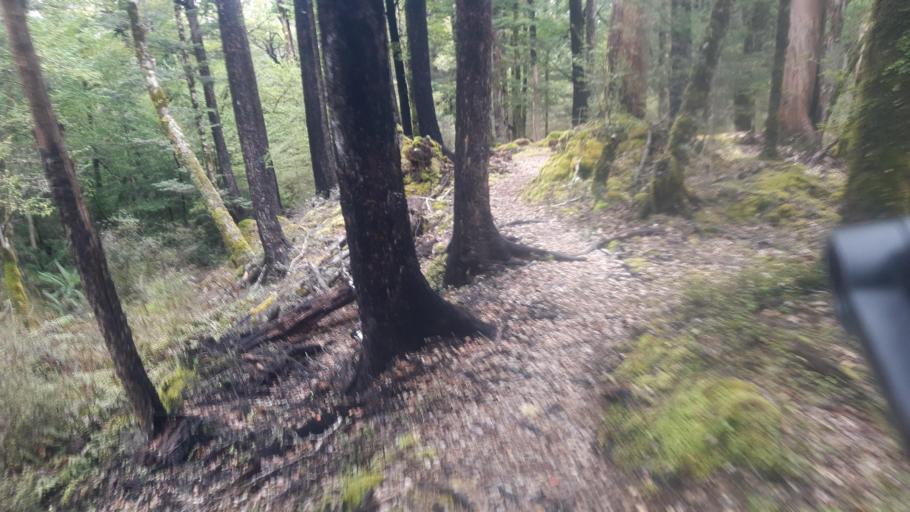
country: NZ
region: Tasman
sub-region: Tasman District
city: Wakefield
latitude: -41.7737
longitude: 172.8073
